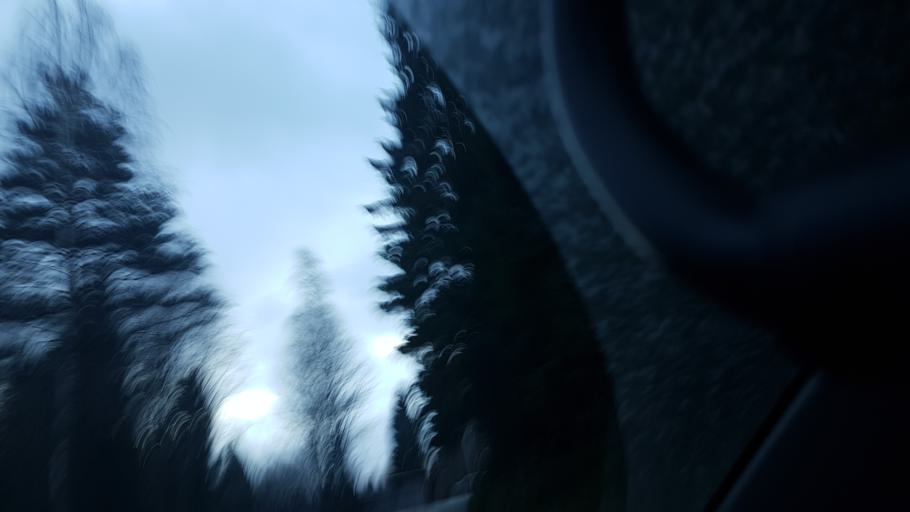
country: FI
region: Uusimaa
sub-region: Helsinki
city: Lohja
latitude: 60.2152
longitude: 24.0899
